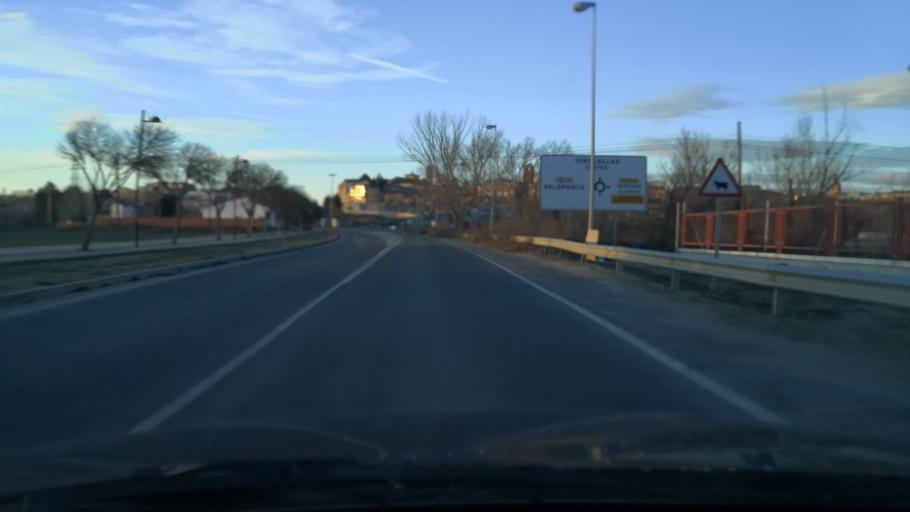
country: ES
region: Castille and Leon
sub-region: Provincia de Valladolid
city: Tordesillas
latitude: 41.4947
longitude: -4.9988
